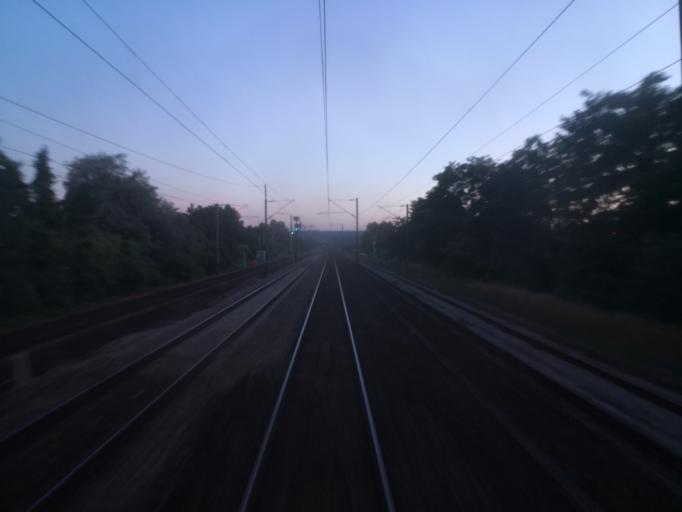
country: FR
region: Ile-de-France
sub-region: Departement des Yvelines
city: Acheres
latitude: 48.9431
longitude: 2.0633
